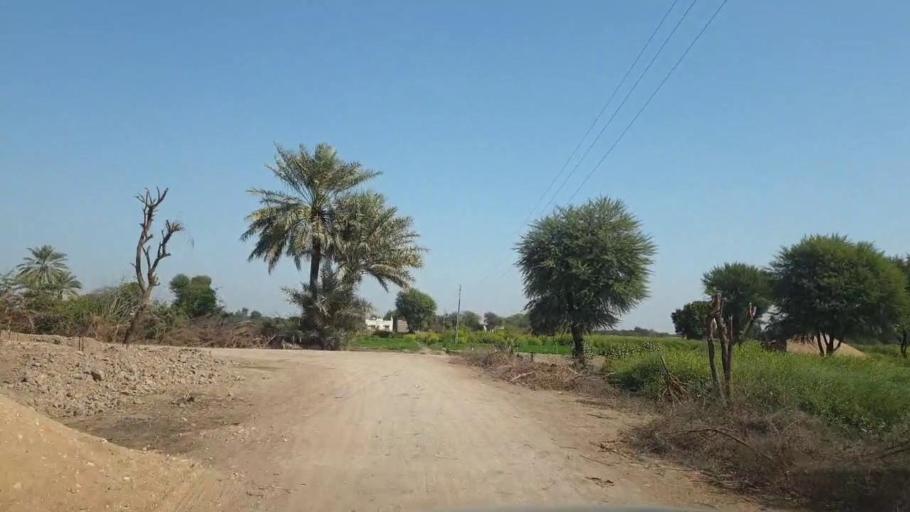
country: PK
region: Sindh
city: Tando Adam
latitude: 25.6445
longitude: 68.6849
